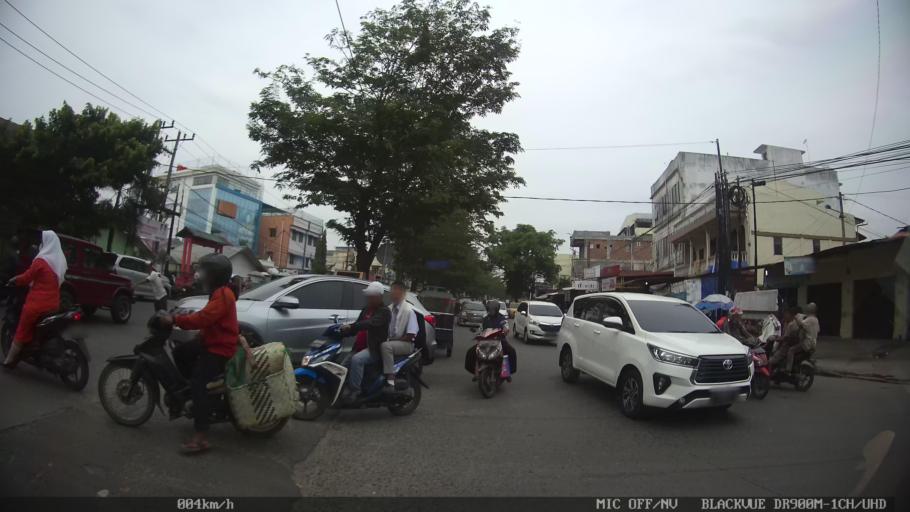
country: ID
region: North Sumatra
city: Deli Tua
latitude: 3.5493
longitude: 98.6984
